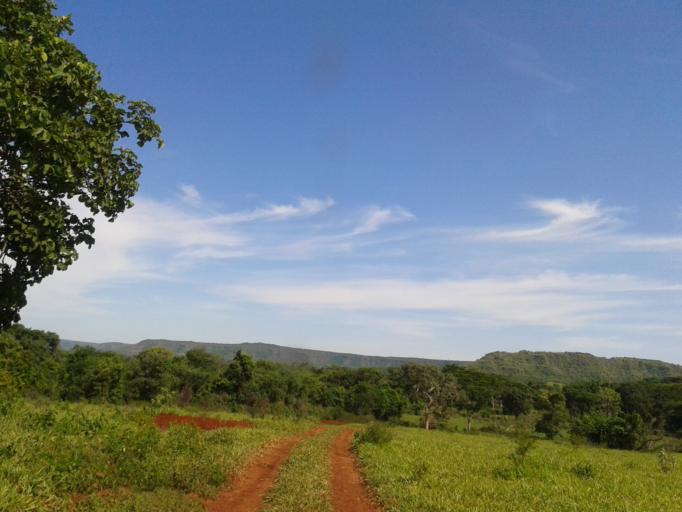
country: BR
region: Minas Gerais
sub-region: Santa Vitoria
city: Santa Vitoria
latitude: -19.0921
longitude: -50.0155
